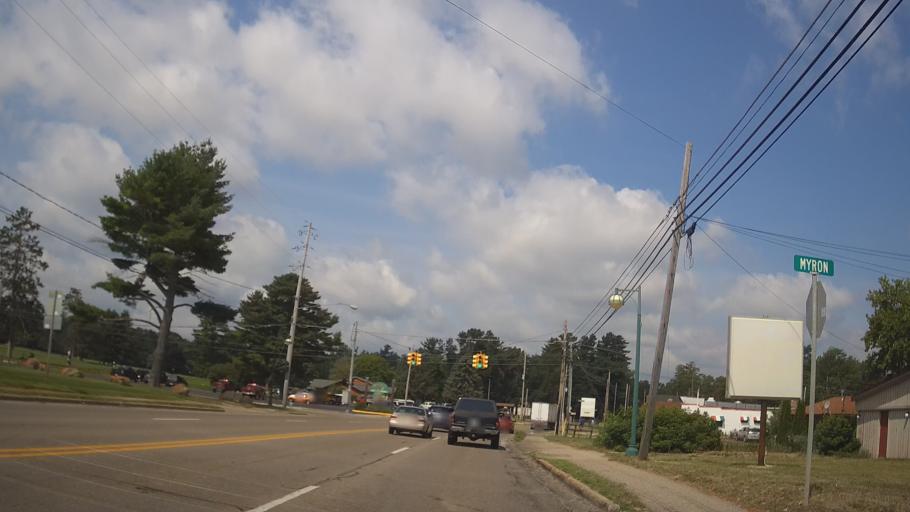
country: US
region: Michigan
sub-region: Roscommon County
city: Houghton Lake
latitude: 44.2983
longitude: -84.7324
